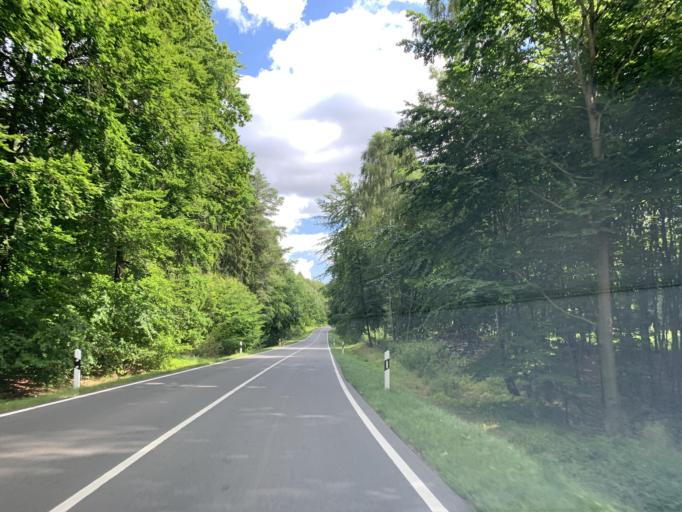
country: DE
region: Mecklenburg-Vorpommern
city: Wustrow
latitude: 53.4170
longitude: 13.1748
